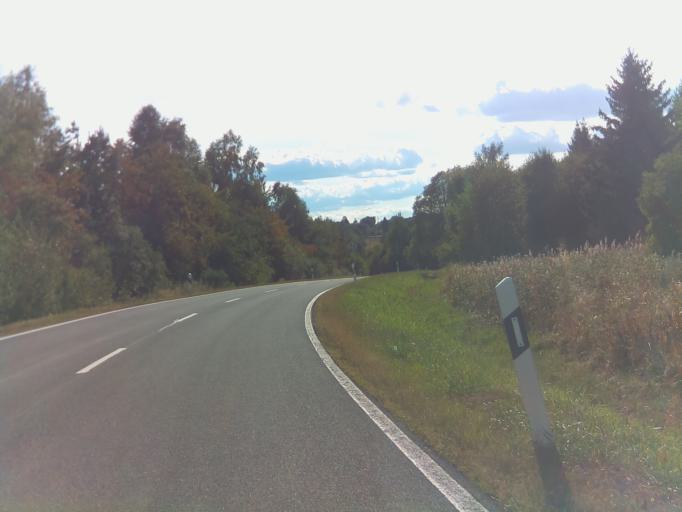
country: DE
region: Thuringia
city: Birx
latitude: 50.5198
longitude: 10.0653
